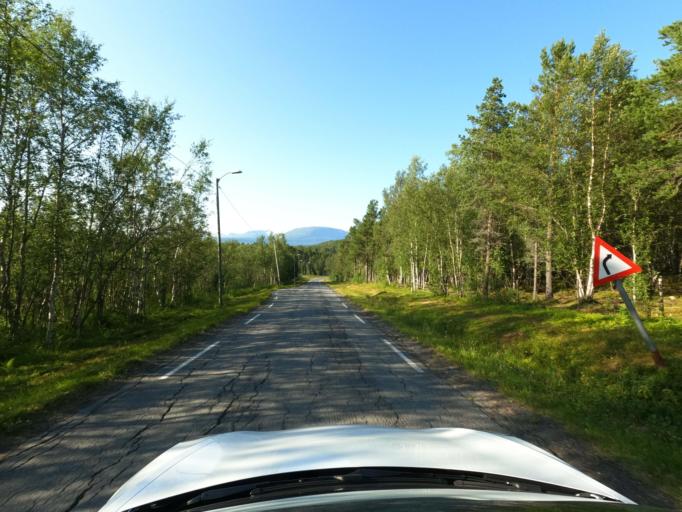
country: NO
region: Nordland
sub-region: Narvik
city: Bjerkvik
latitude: 68.4806
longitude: 17.5276
